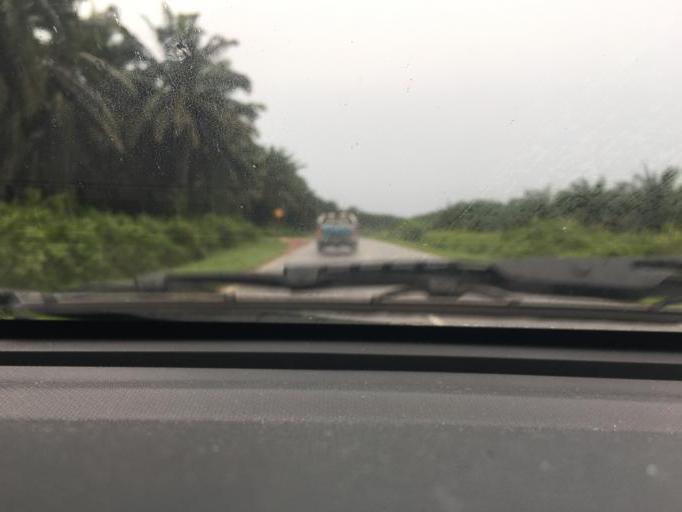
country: MY
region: Kedah
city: Bedong
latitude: 5.6563
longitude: 100.6323
